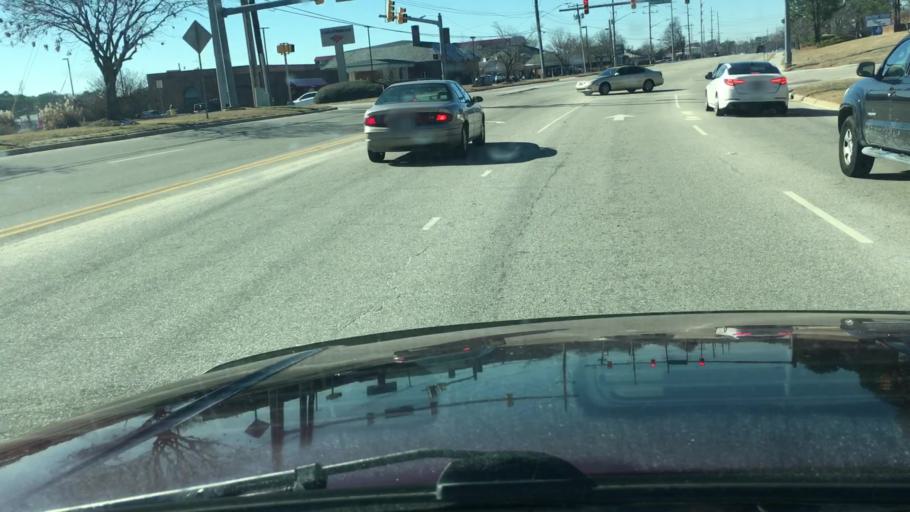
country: US
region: North Carolina
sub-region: Cumberland County
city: Fayetteville
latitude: 35.0321
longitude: -78.9241
